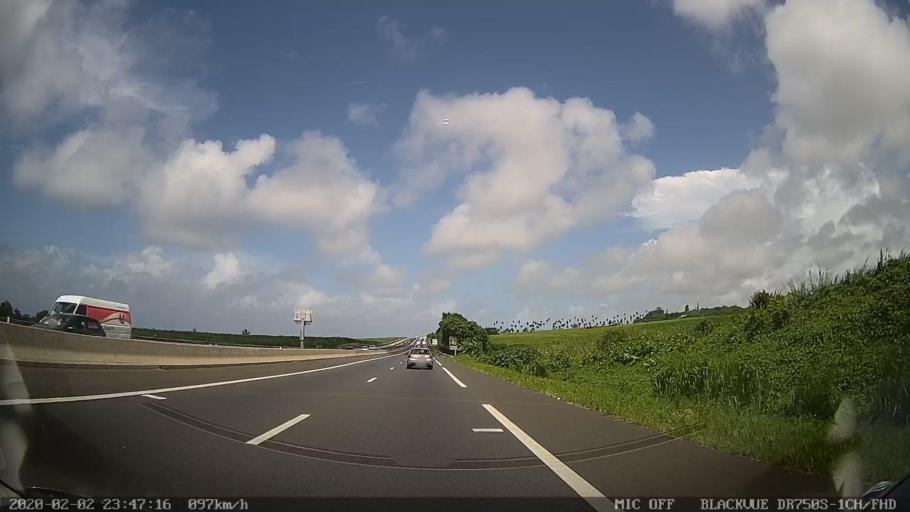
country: RE
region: Reunion
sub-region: Reunion
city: Sainte-Suzanne
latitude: -20.8998
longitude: 55.5824
